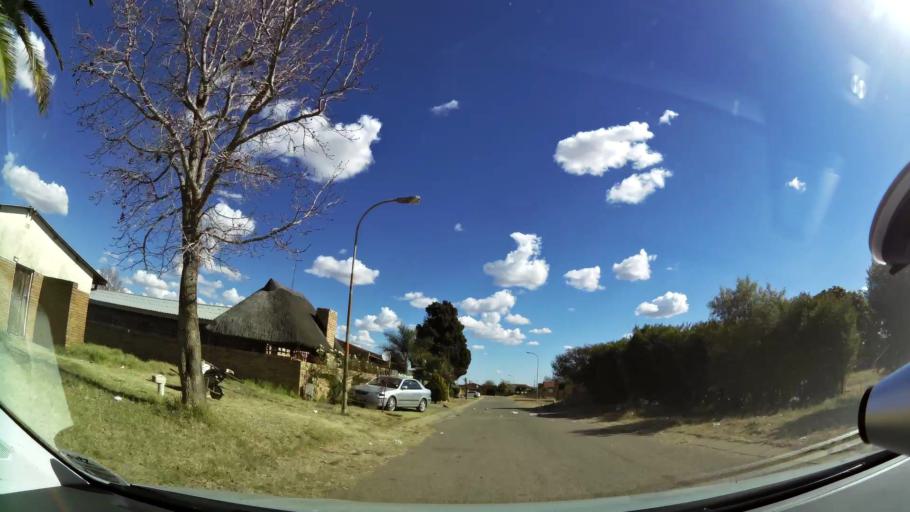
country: ZA
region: North-West
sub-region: Dr Kenneth Kaunda District Municipality
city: Klerksdorp
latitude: -26.8718
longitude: 26.5832
